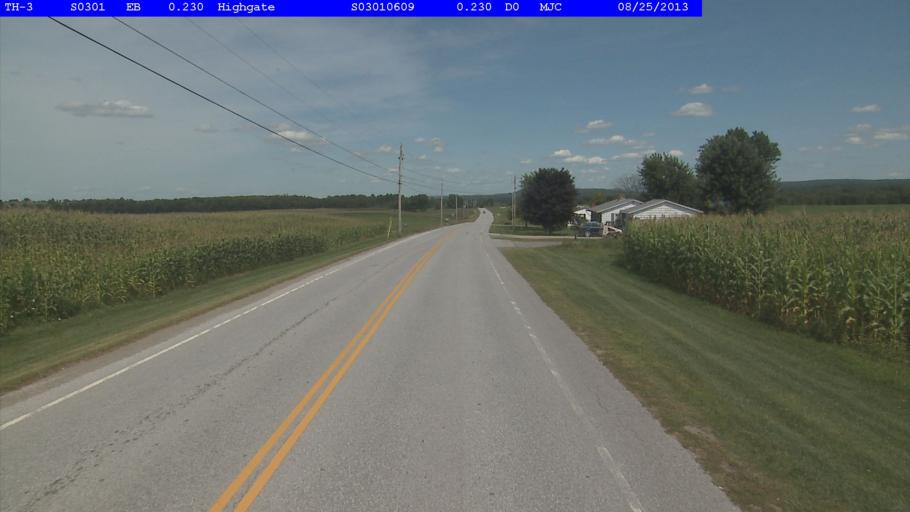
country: US
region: Vermont
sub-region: Franklin County
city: Swanton
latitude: 44.9488
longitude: -73.0116
